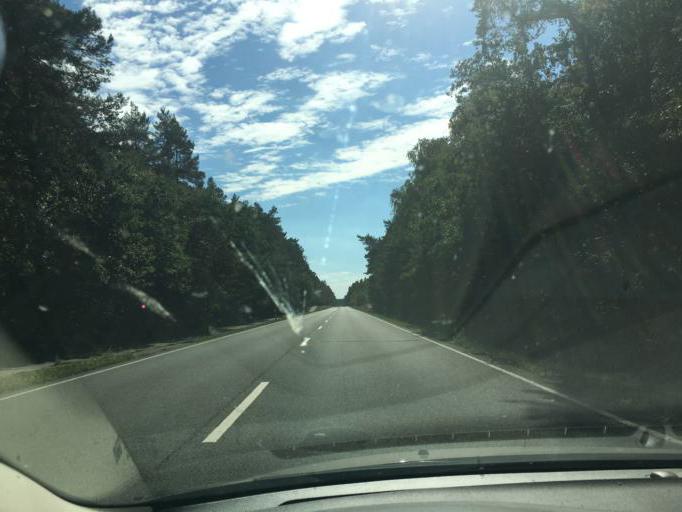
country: DE
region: Saxony-Anhalt
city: Seehausen
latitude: 52.8508
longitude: 11.7319
